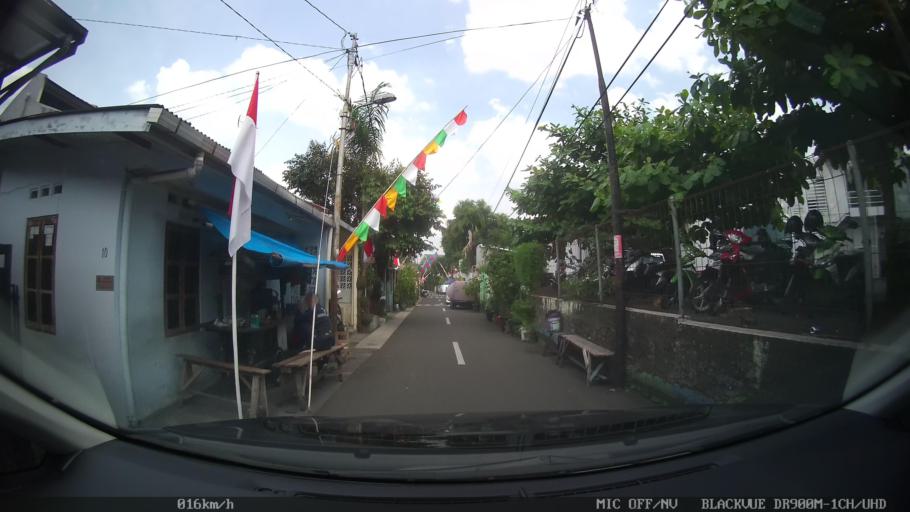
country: ID
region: Daerah Istimewa Yogyakarta
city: Yogyakarta
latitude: -7.7832
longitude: 110.3832
